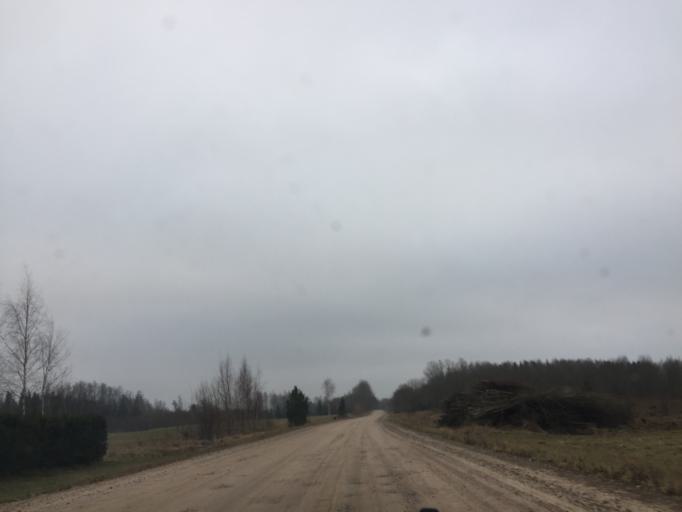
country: LV
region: Limbazu Rajons
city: Limbazi
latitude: 57.6017
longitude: 24.6127
